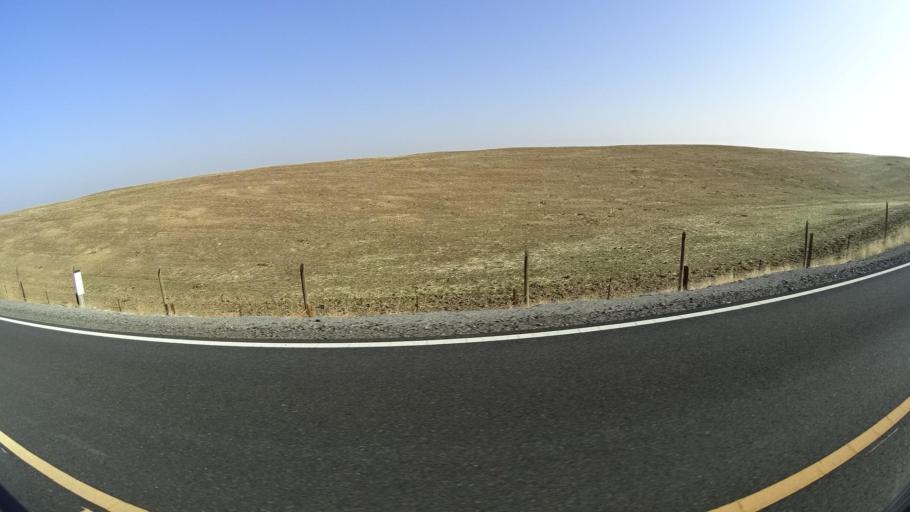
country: US
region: California
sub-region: Tulare County
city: Richgrove
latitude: 35.7586
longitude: -119.0251
